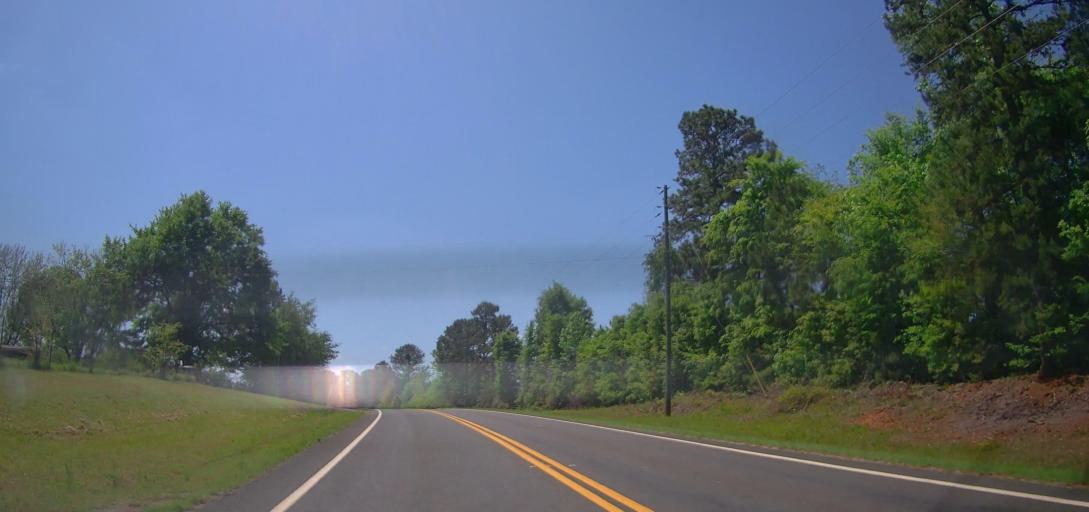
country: US
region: Georgia
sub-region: Jasper County
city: Monticello
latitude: 33.2752
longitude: -83.6001
